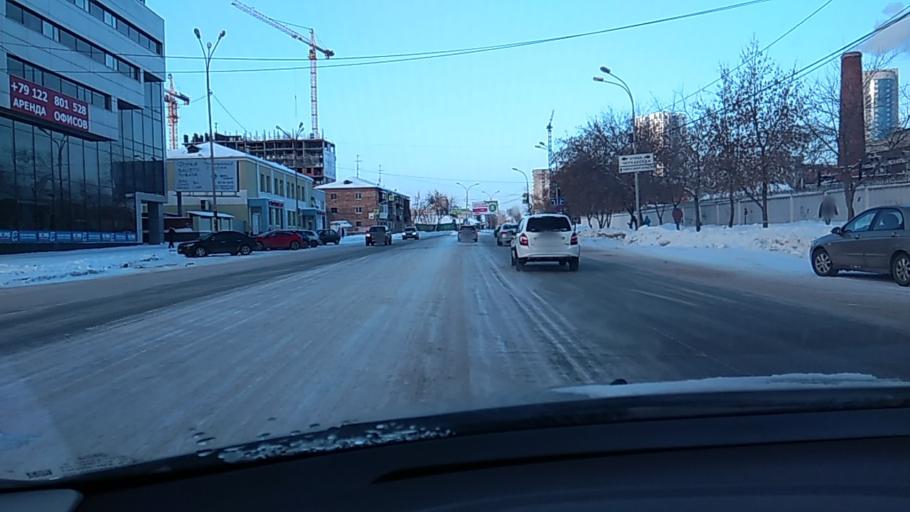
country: RU
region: Sverdlovsk
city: Sovkhoznyy
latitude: 56.8197
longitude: 60.5562
